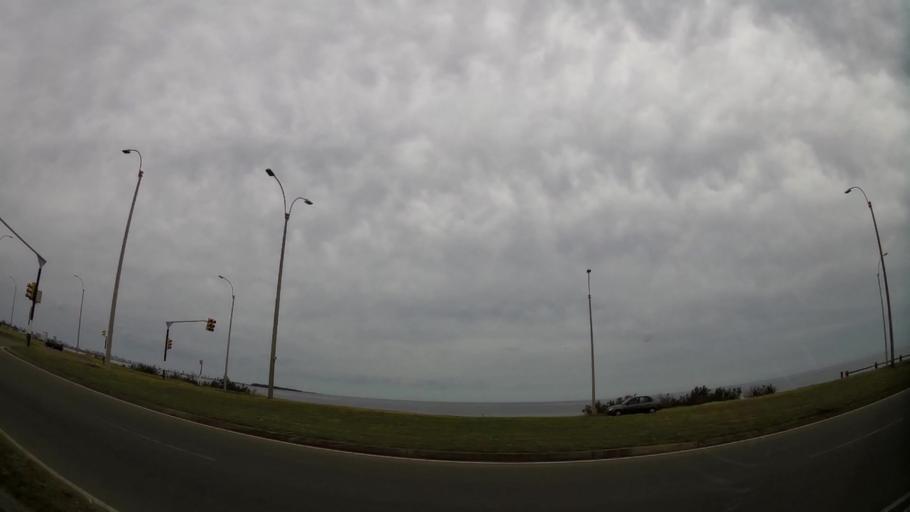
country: UY
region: Maldonado
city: Maldonado
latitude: -34.9091
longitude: -55.0046
